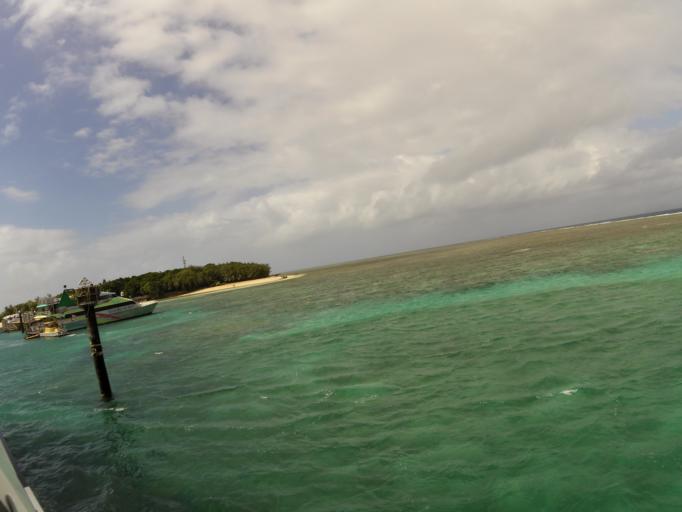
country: AU
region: Queensland
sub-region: Cairns
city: Yorkeys Knob
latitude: -16.7580
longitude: 145.9679
